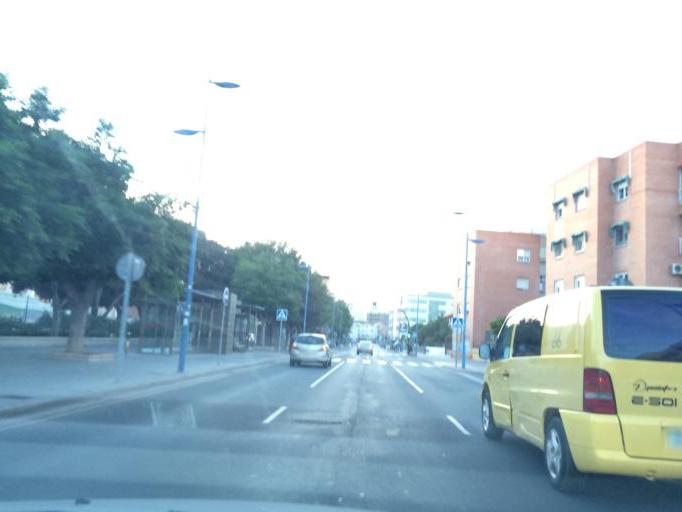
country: ES
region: Andalusia
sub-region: Provincia de Almeria
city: Almeria
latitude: 36.8395
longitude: -2.4503
